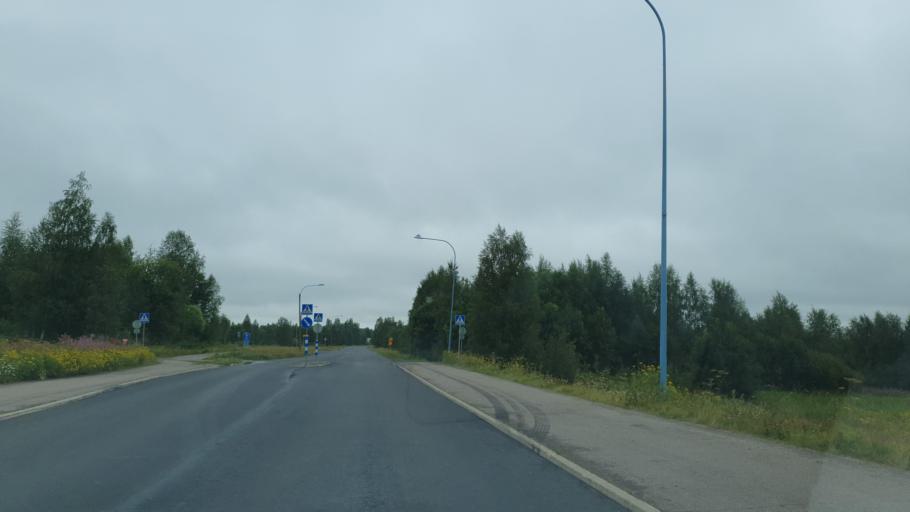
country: FI
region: Lapland
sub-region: Itae-Lappi
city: Pelkosenniemi
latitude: 67.1134
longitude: 27.5116
